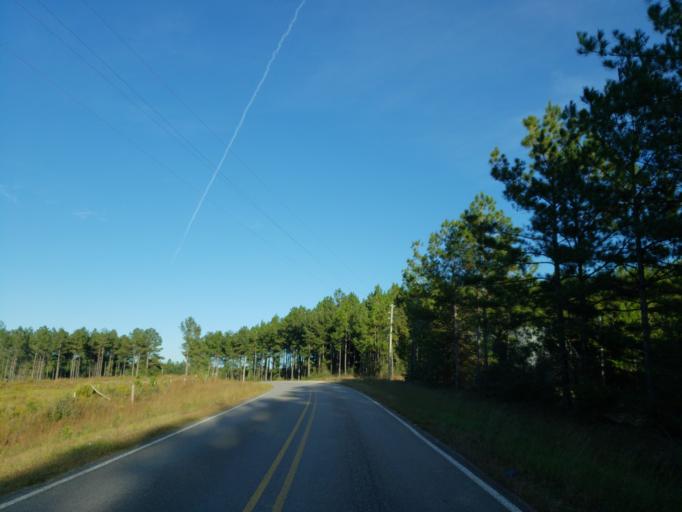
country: US
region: Mississippi
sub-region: Perry County
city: Richton
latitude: 31.3407
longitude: -88.7929
